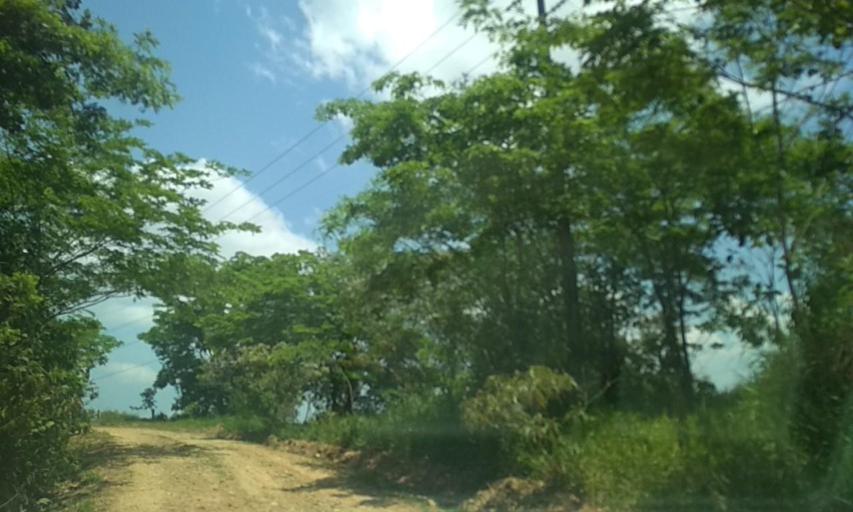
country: MX
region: Chiapas
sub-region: Tecpatan
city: Raudales Malpaso
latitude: 17.3943
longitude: -93.7400
